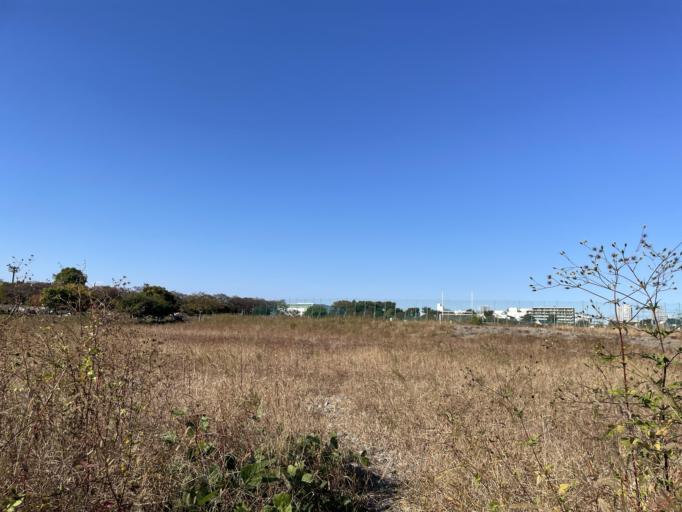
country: JP
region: Tokyo
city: Kokubunji
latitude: 35.6528
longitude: 139.4798
